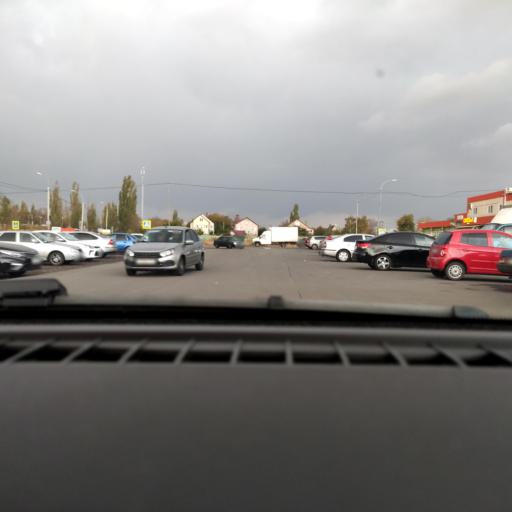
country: RU
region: Voronezj
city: Maslovka
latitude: 51.6137
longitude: 39.2584
